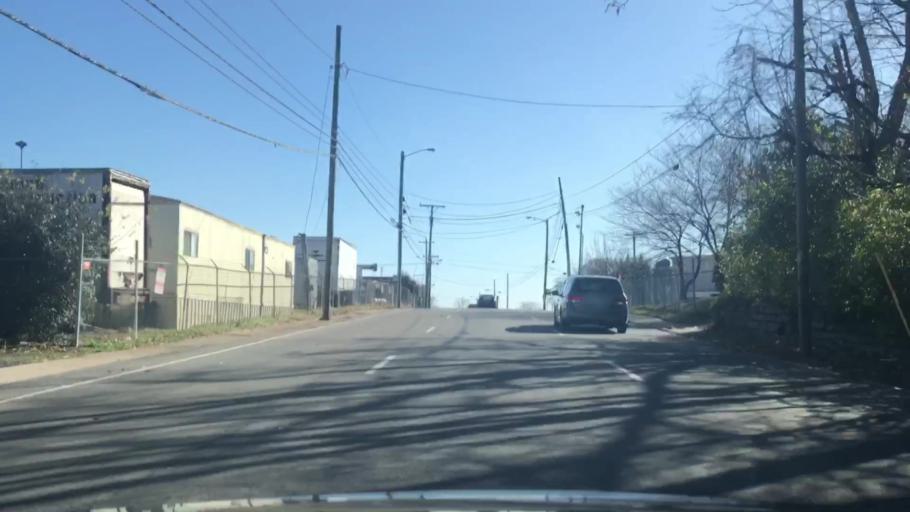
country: US
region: Tennessee
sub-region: Davidson County
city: Nashville
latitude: 36.1413
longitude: -86.7643
